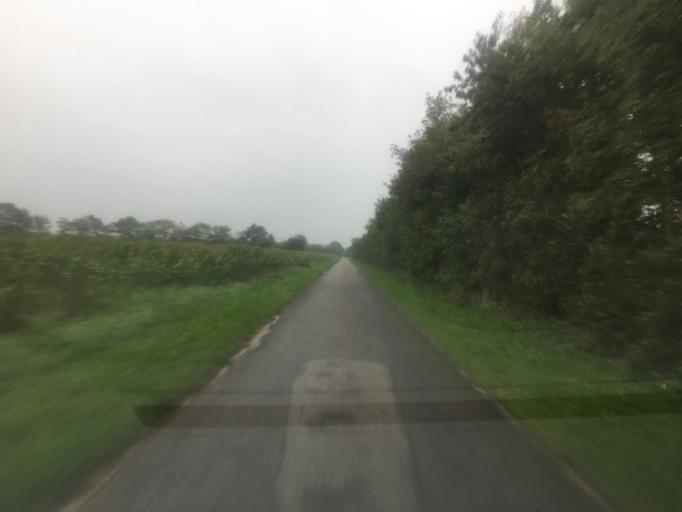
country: DK
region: South Denmark
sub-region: Tonder Kommune
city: Logumkloster
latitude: 55.0413
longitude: 8.9195
